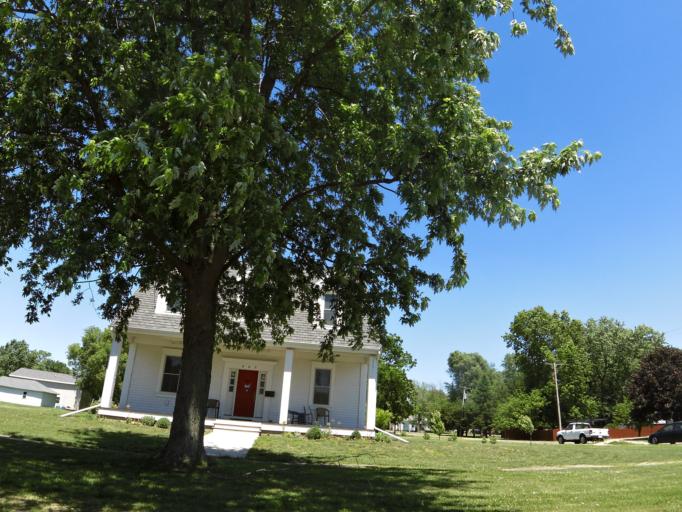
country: US
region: Illinois
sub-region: Iroquois County
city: Gilman
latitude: 40.7697
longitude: -87.9957
